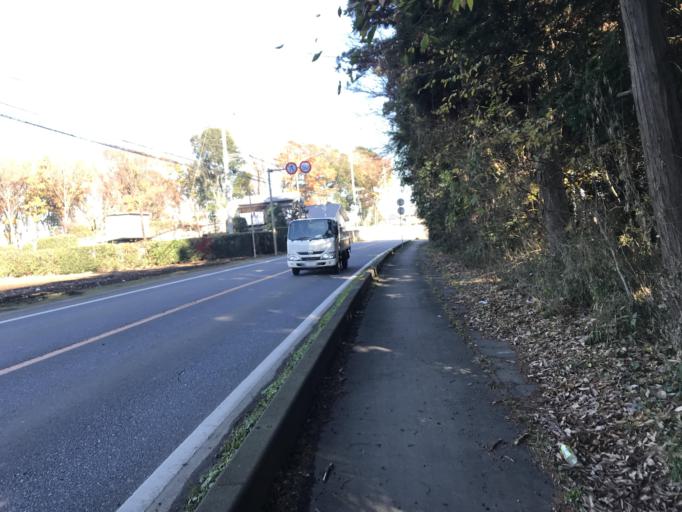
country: JP
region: Tochigi
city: Oyama
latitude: 36.2372
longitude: 139.8263
